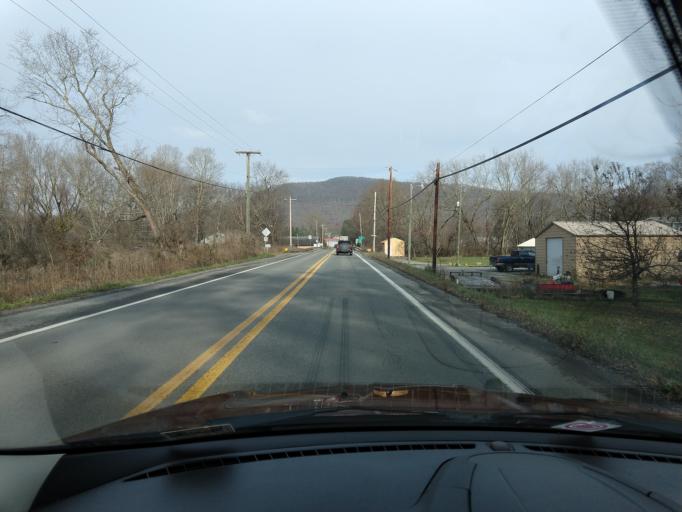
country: US
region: West Virginia
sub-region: Greenbrier County
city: Rainelle
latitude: 37.9574
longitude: -80.6829
